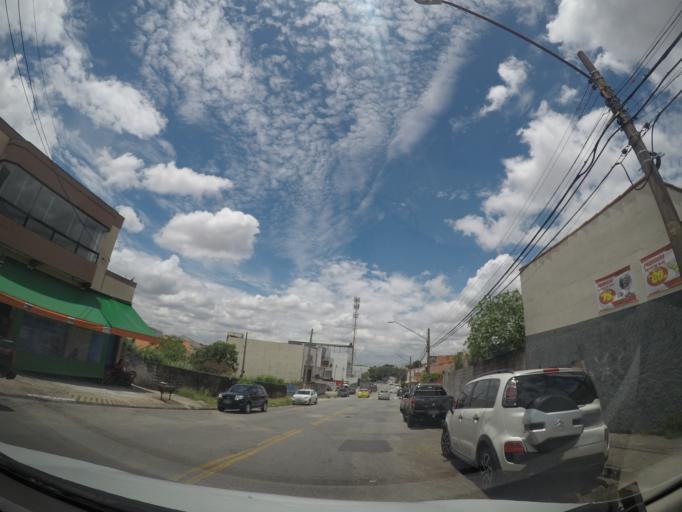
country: BR
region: Sao Paulo
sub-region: Guarulhos
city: Guarulhos
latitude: -23.4461
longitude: -46.5314
